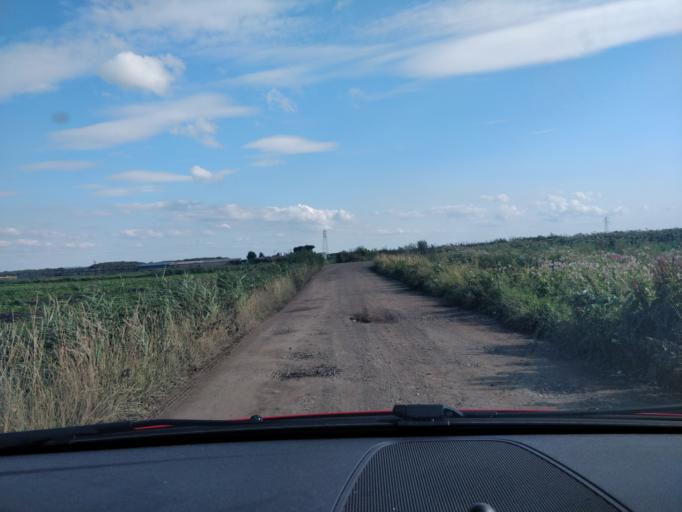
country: GB
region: England
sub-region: Lancashire
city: Banks
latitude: 53.6649
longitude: -2.9187
